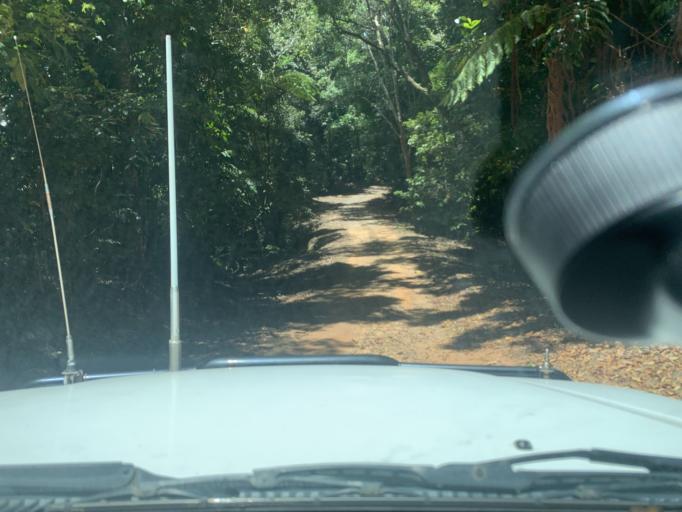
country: AU
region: Queensland
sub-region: Cairns
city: Redlynch
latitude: -16.9585
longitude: 145.6425
